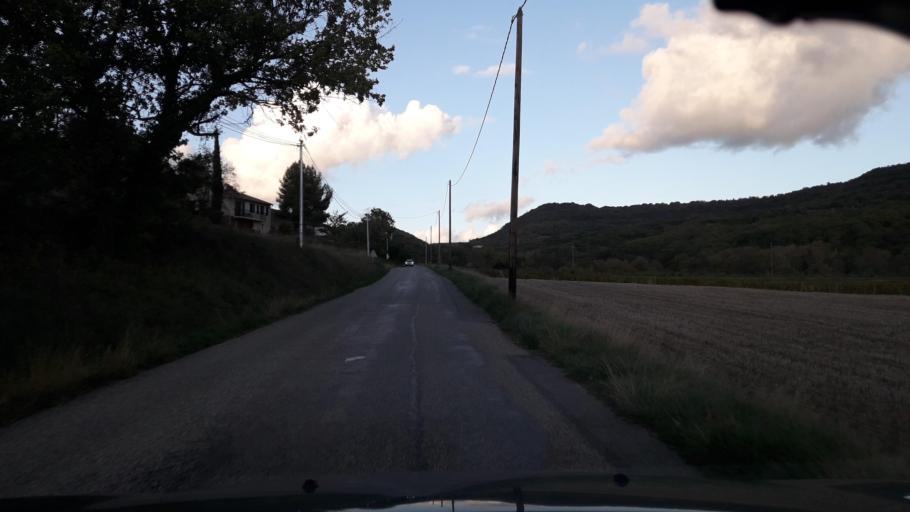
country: FR
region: Rhone-Alpes
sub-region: Departement de l'Ardeche
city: Vesseaux
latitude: 44.6276
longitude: 4.4892
